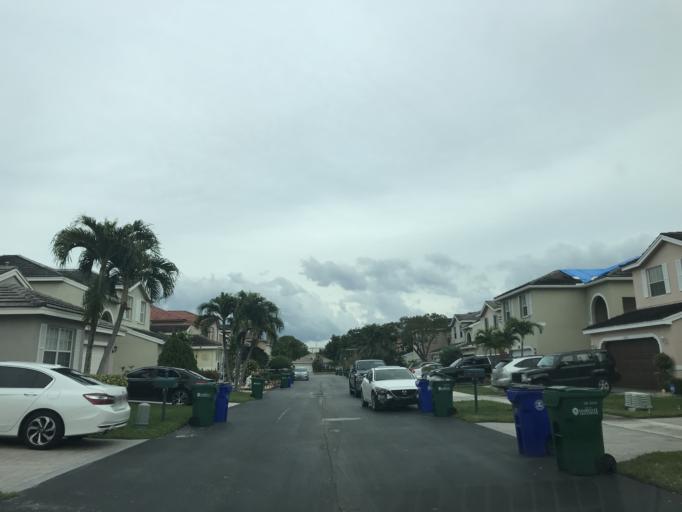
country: US
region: Florida
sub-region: Broward County
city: Margate
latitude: 26.2649
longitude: -80.2044
